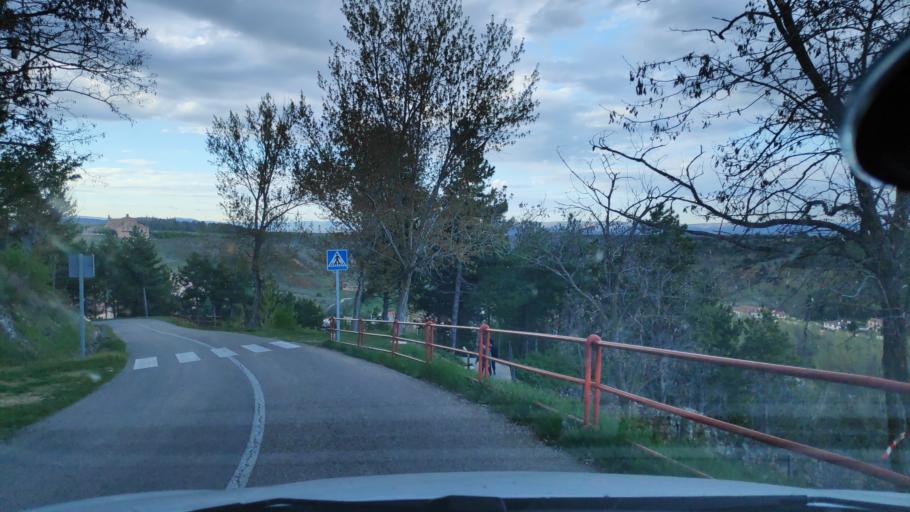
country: ES
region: Castille and Leon
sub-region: Provincia de Soria
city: Soria
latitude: 41.7626
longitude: -2.4567
